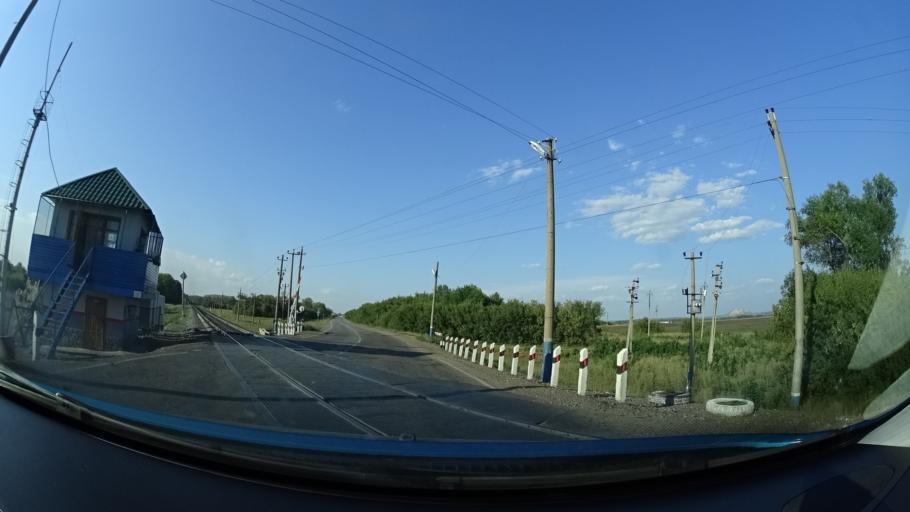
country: RU
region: Bashkortostan
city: Sterlitamak
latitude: 53.5161
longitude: 55.9330
